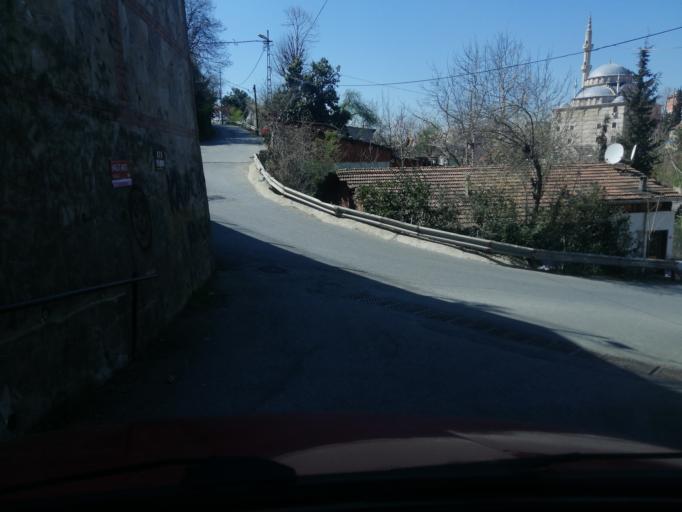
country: TR
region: Istanbul
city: Mahmut Sevket Pasa
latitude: 41.1129
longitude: 29.1128
